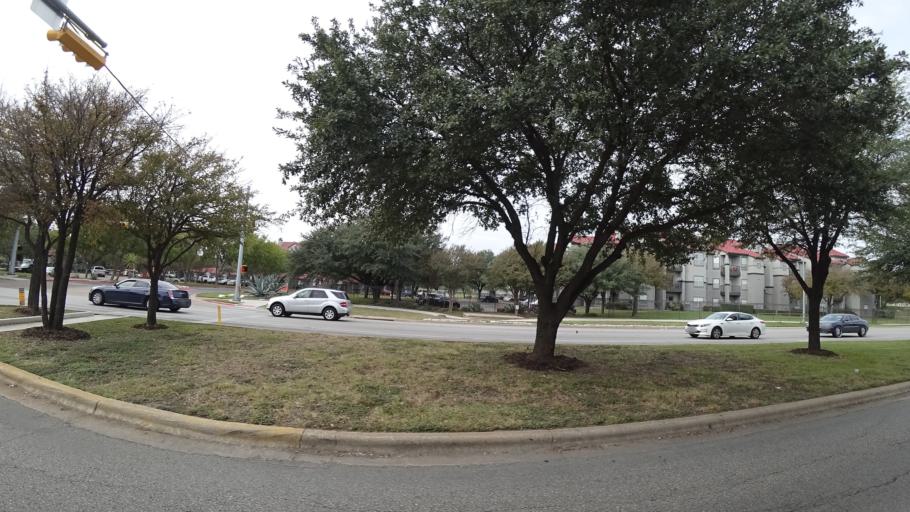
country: US
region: Texas
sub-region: Travis County
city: Wells Branch
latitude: 30.4389
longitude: -97.6718
